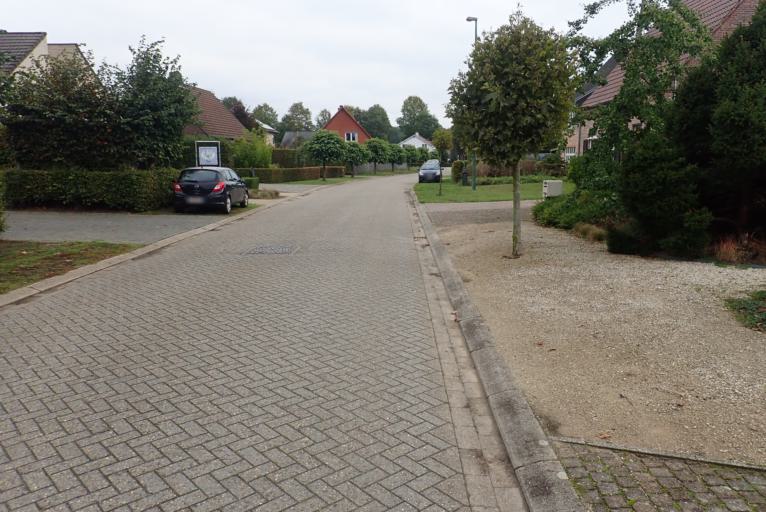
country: BE
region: Flanders
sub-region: Provincie Antwerpen
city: Vorselaar
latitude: 51.2074
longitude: 4.7658
